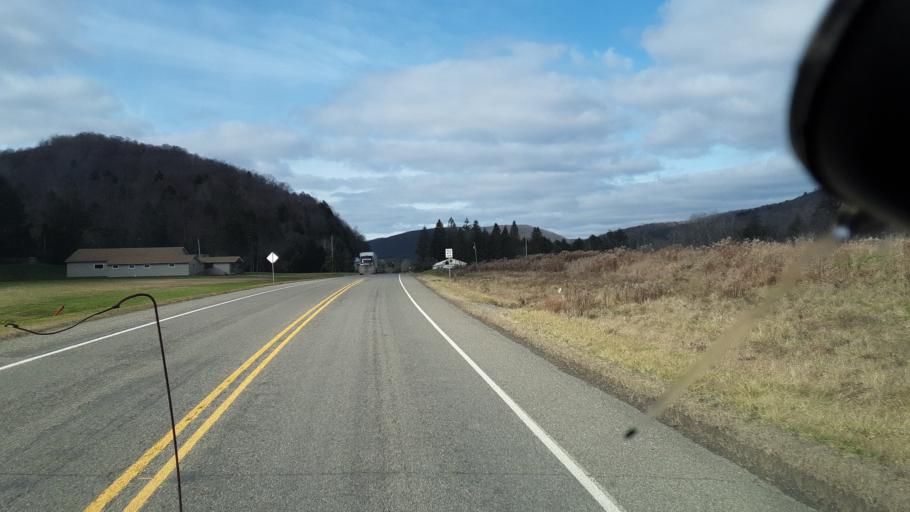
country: US
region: Pennsylvania
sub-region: Potter County
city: Galeton
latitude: 41.7821
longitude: -77.7402
